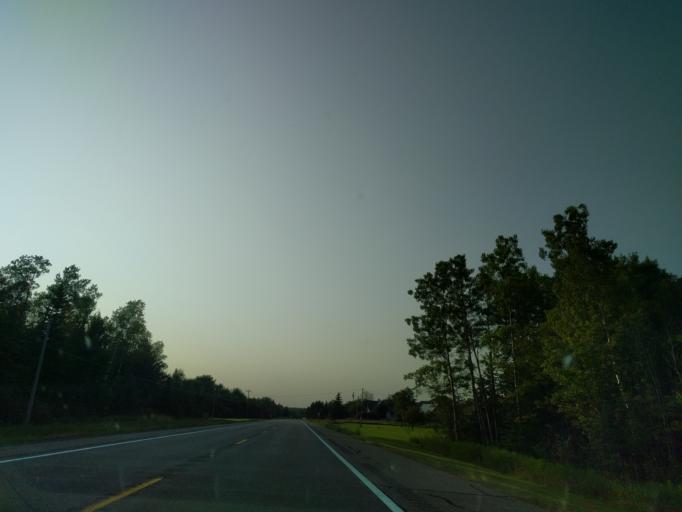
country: US
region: Michigan
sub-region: Marquette County
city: Harvey
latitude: 46.4135
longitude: -87.2519
